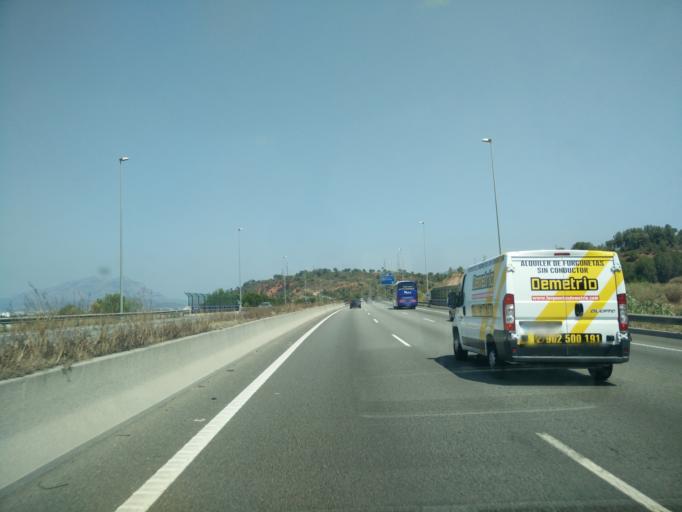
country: ES
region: Catalonia
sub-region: Provincia de Barcelona
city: Martorell
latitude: 41.4791
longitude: 1.9367
